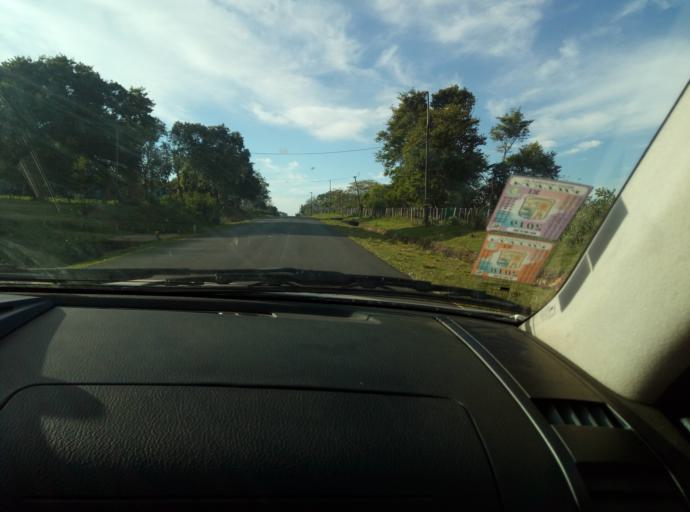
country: PY
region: Caaguazu
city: Carayao
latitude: -25.1624
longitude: -56.3123
